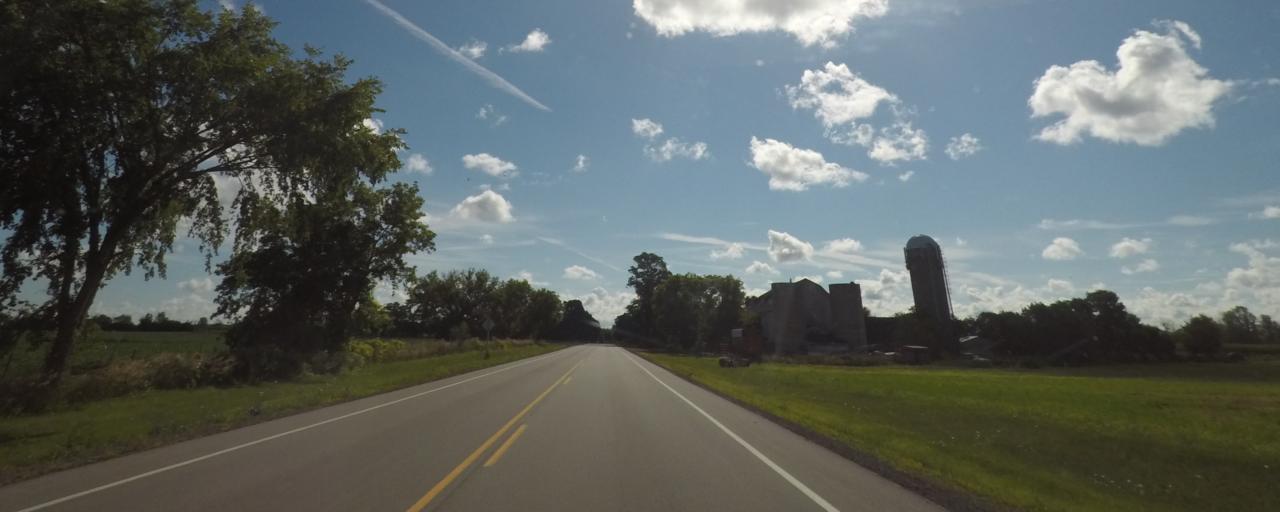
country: US
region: Wisconsin
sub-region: Jefferson County
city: Ixonia
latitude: 43.0756
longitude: -88.5695
